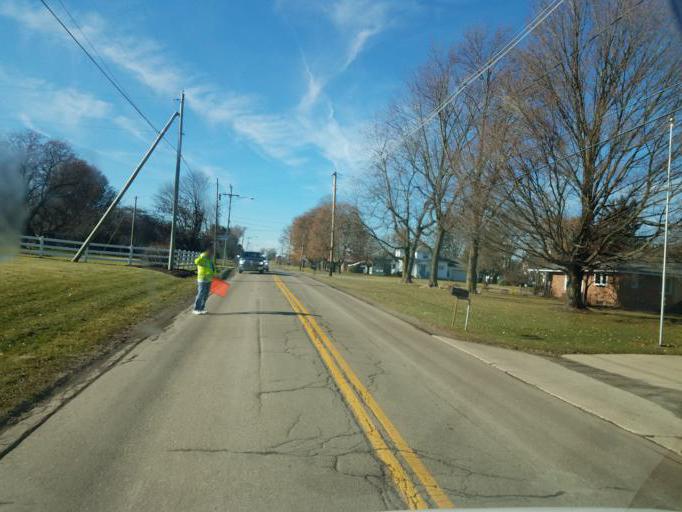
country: US
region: Ohio
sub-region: Wayne County
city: Dalton
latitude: 40.7412
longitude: -81.7538
